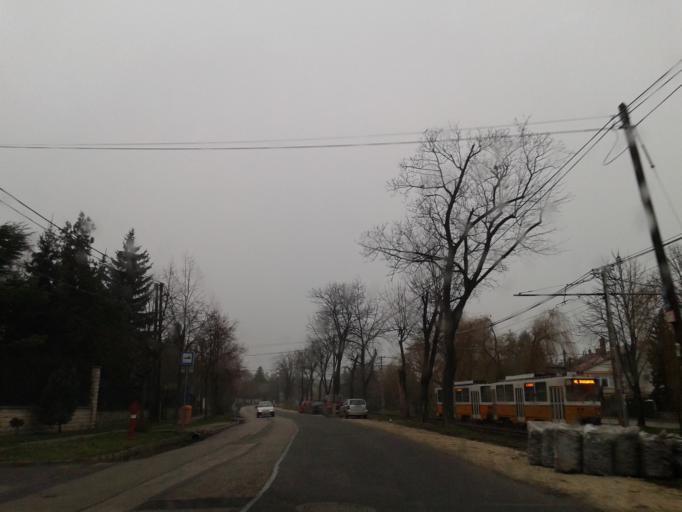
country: HU
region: Budapest
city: Budapest XXII. keruelet
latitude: 47.4383
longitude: 19.0304
